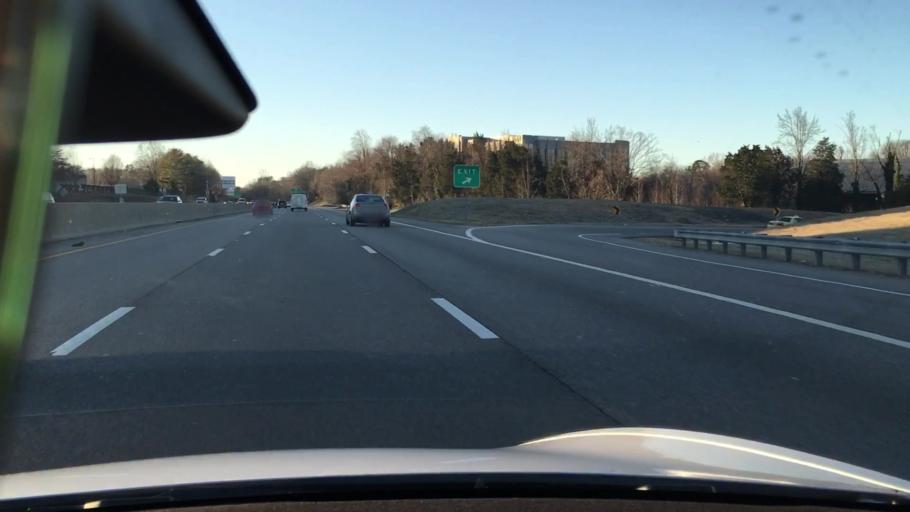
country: US
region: Virginia
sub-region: Chesterfield County
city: Bon Air
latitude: 37.5157
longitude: -77.5283
